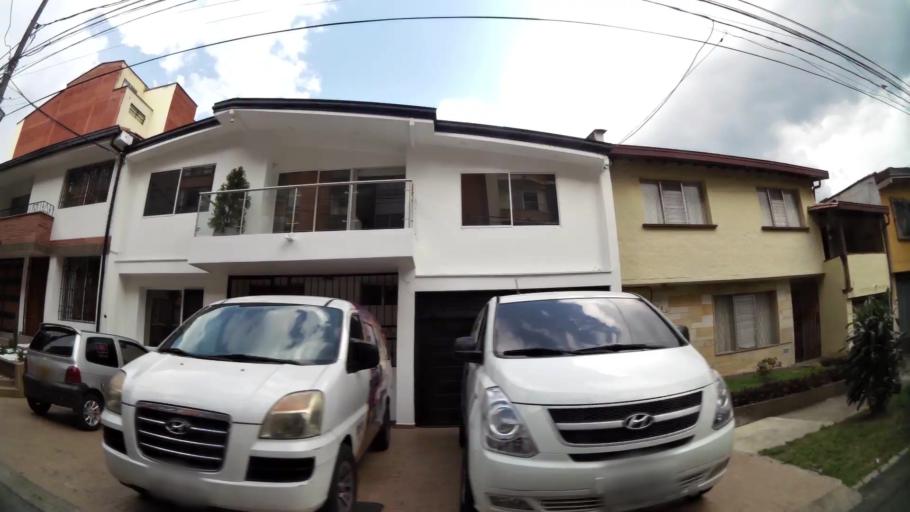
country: CO
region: Antioquia
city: Medellin
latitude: 6.2532
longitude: -75.5943
